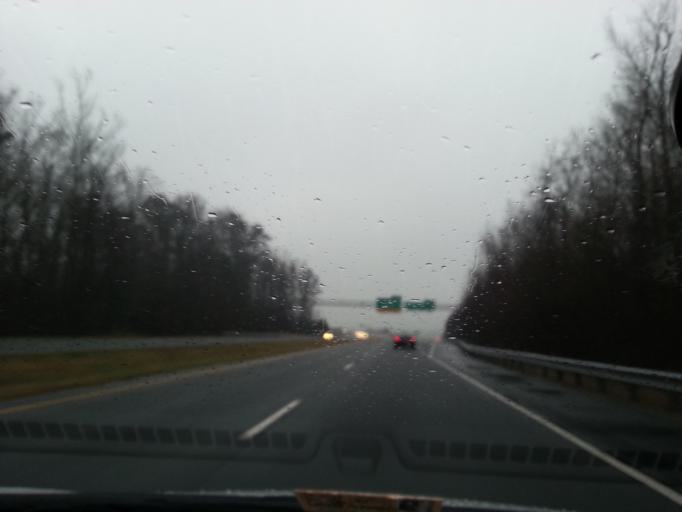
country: US
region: North Carolina
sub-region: Currituck County
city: Moyock
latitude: 36.6639
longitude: -76.2305
